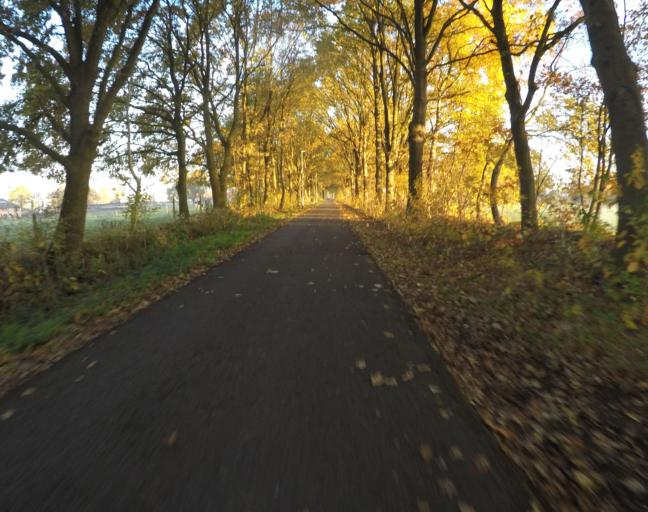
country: BE
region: Flanders
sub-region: Provincie Antwerpen
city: Hulshout
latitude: 51.0859
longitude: 4.8253
